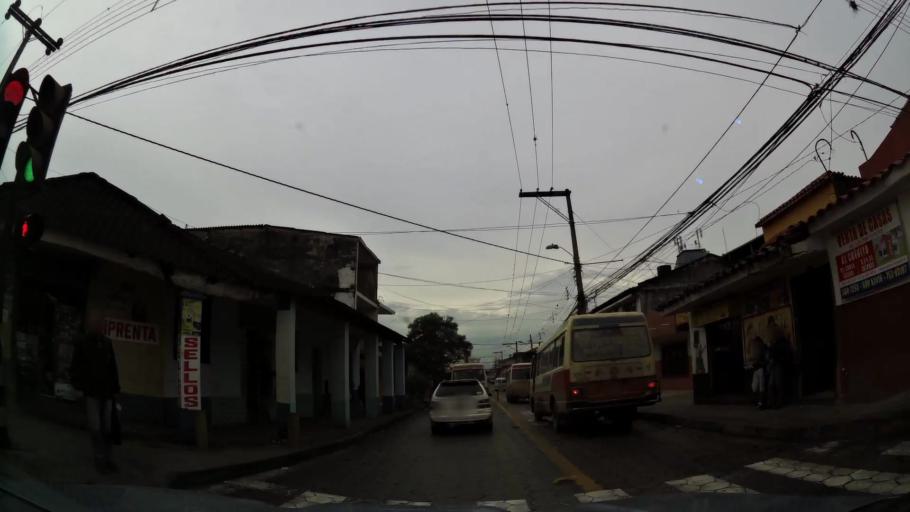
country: BO
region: Santa Cruz
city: Santa Cruz de la Sierra
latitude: -17.7888
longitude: -63.1851
